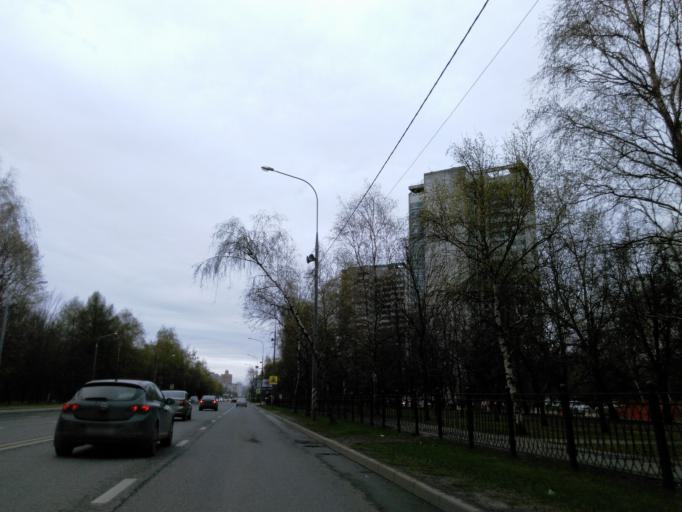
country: RU
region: Moskovskaya
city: Levoberezhnyy
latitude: 55.8559
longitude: 37.4508
